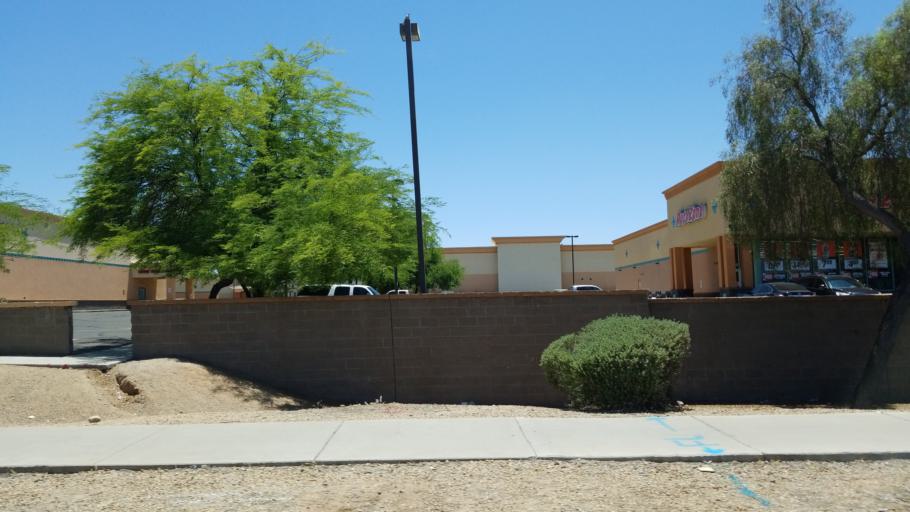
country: US
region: Arizona
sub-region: Maricopa County
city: Glendale
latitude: 33.5087
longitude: -112.2391
